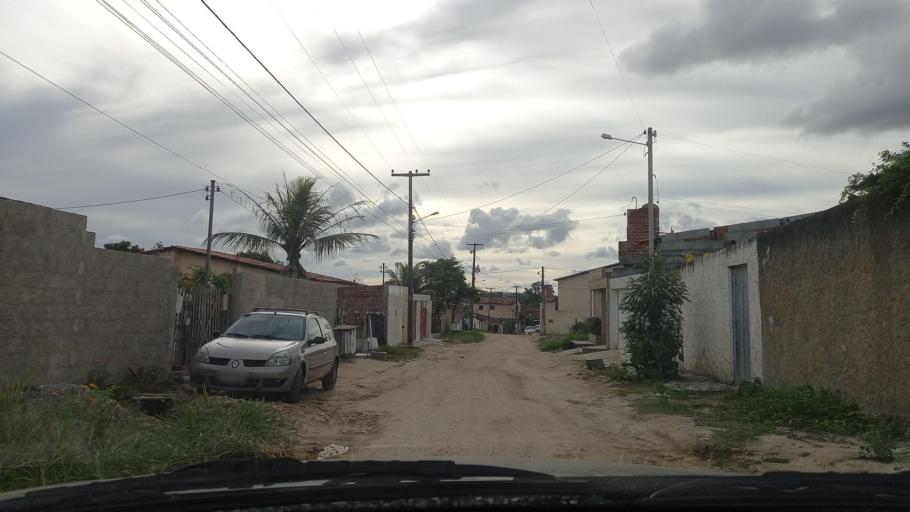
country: BR
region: Pernambuco
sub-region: Gravata
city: Gravata
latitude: -8.2000
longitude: -35.5377
